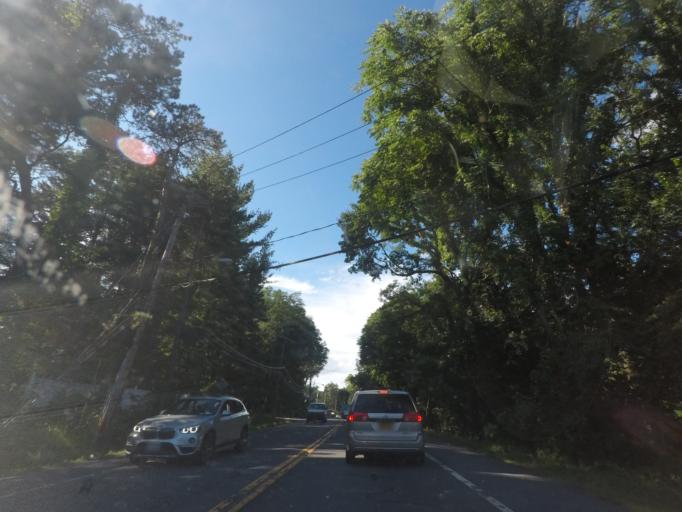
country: US
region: New York
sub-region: Albany County
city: West Albany
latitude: 42.6941
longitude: -73.7531
